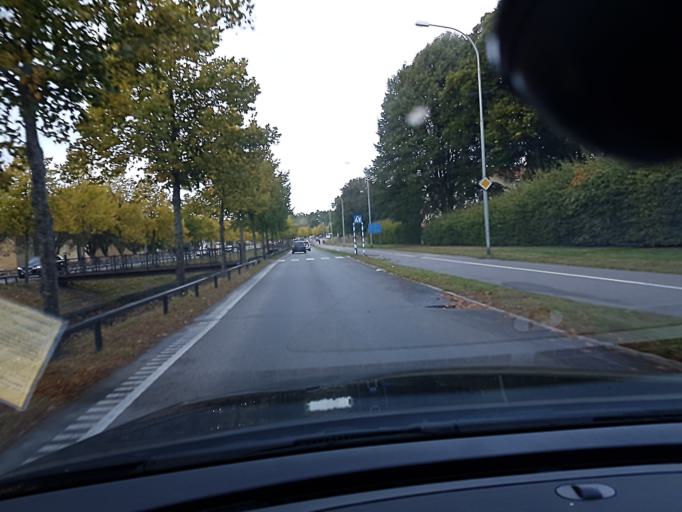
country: SE
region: Kronoberg
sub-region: Vaxjo Kommun
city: Vaexjoe
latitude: 56.8833
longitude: 14.8125
